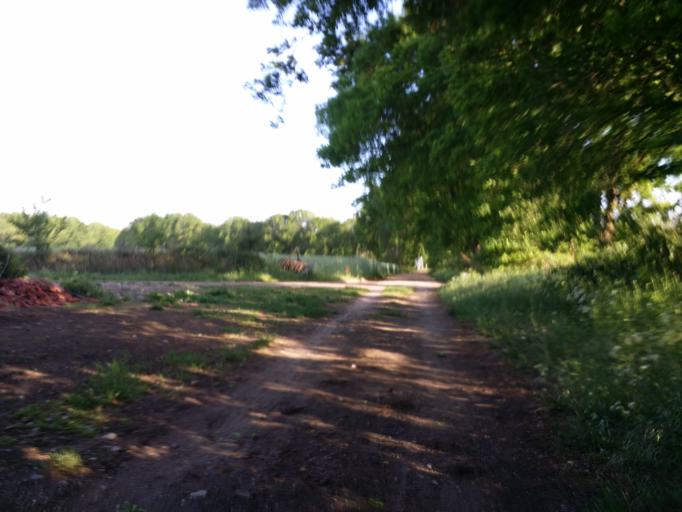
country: DE
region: Lower Saxony
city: Ganderkesee
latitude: 53.0128
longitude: 8.5524
